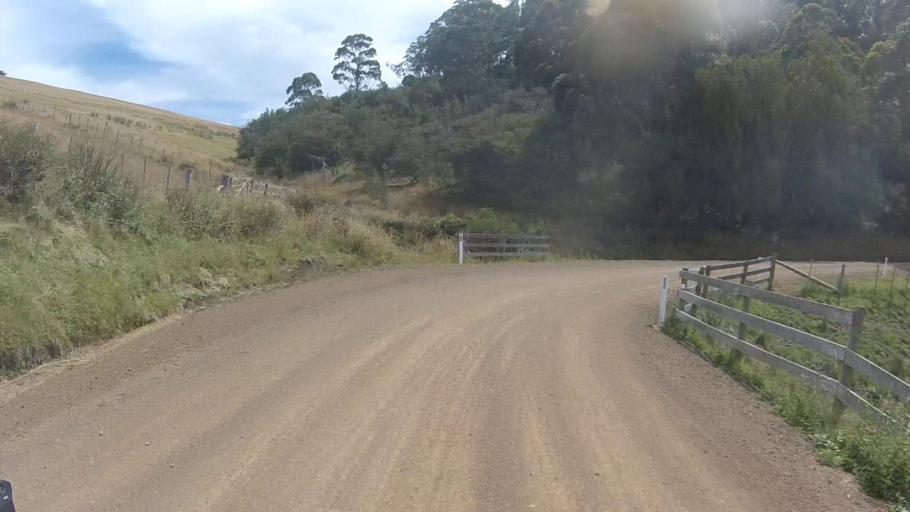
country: AU
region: Tasmania
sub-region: Sorell
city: Sorell
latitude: -42.7935
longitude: 147.8418
